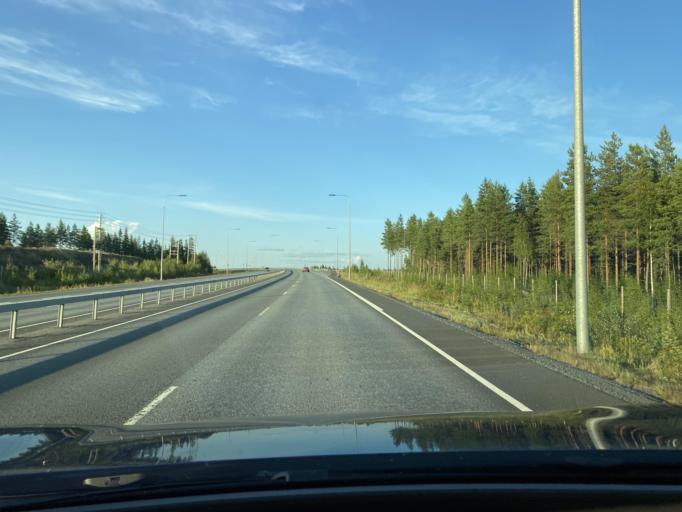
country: FI
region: Southern Ostrobothnia
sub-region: Seinaejoki
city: Nurmo
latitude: 62.7363
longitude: 22.9084
